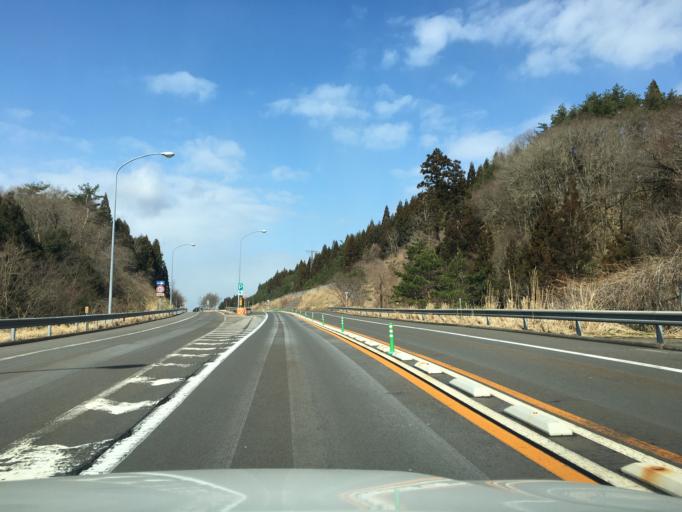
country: JP
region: Akita
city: Akita
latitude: 39.7473
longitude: 140.1561
